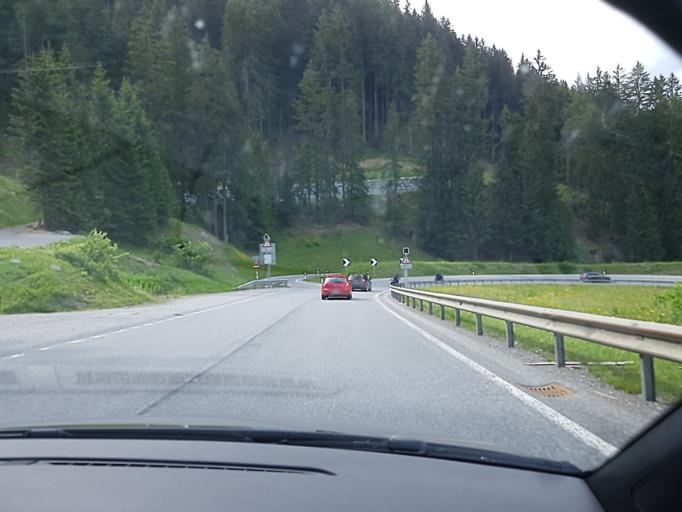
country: CH
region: Grisons
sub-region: Praettigau/Davos District
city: Klosters Serneus
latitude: 46.8592
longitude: 9.8786
